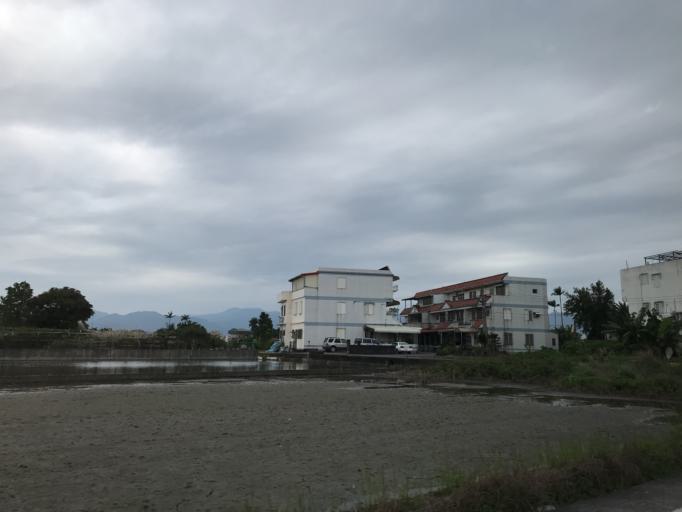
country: TW
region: Taiwan
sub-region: Yilan
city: Yilan
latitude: 24.6887
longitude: 121.7865
